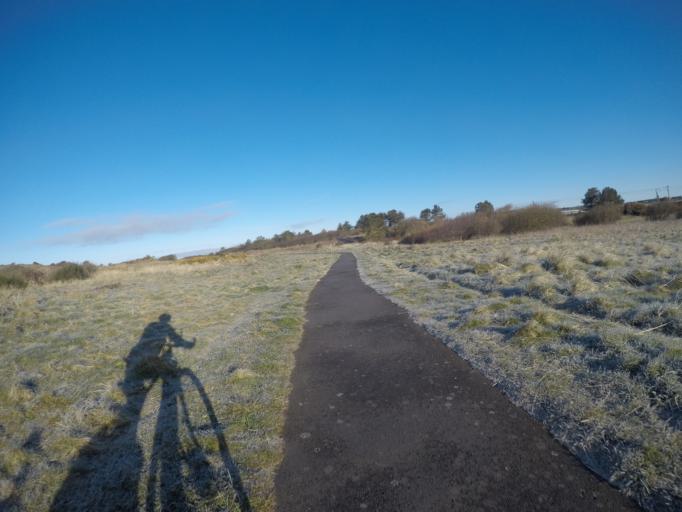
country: GB
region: Scotland
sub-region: North Ayrshire
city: Stevenston
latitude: 55.6316
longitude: -4.7588
